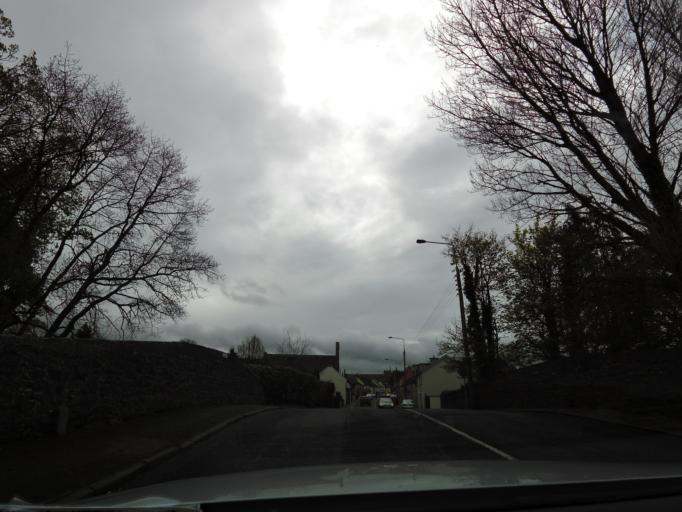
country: IE
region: Leinster
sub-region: Kilkenny
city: Ballyragget
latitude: 52.7336
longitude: -7.3982
